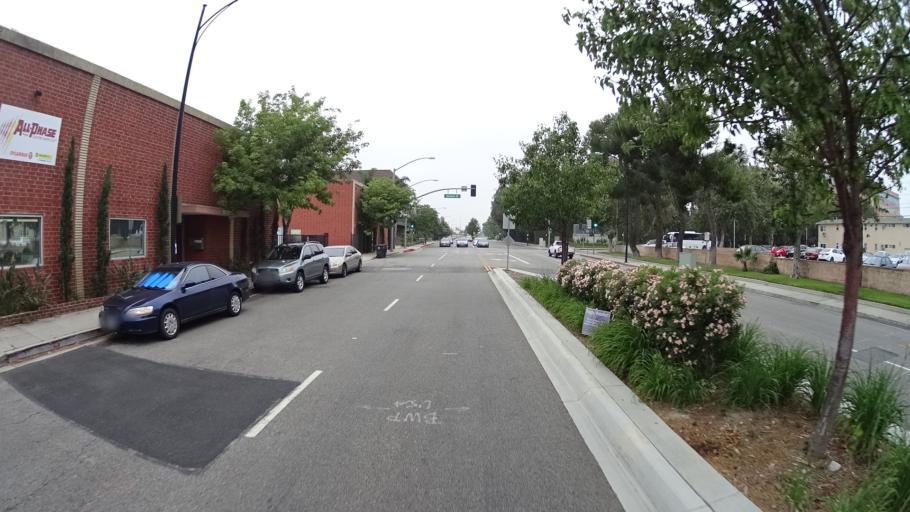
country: US
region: California
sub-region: Los Angeles County
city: Burbank
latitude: 34.1918
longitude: -118.3439
